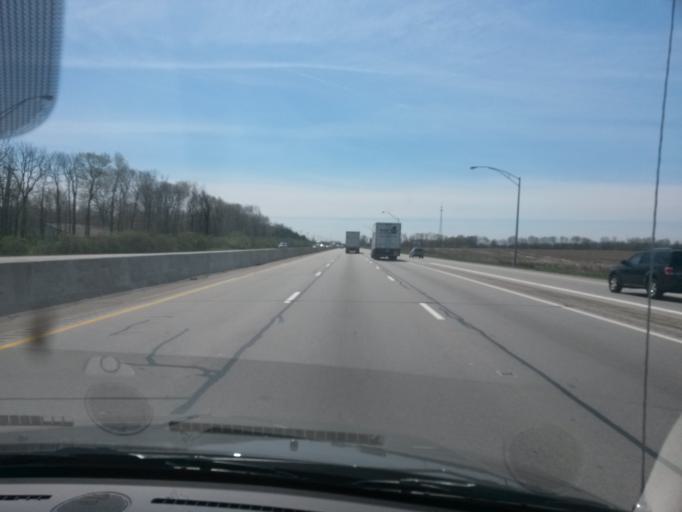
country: US
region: Ohio
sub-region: Miami County
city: Tipp City
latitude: 39.9576
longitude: -84.1895
